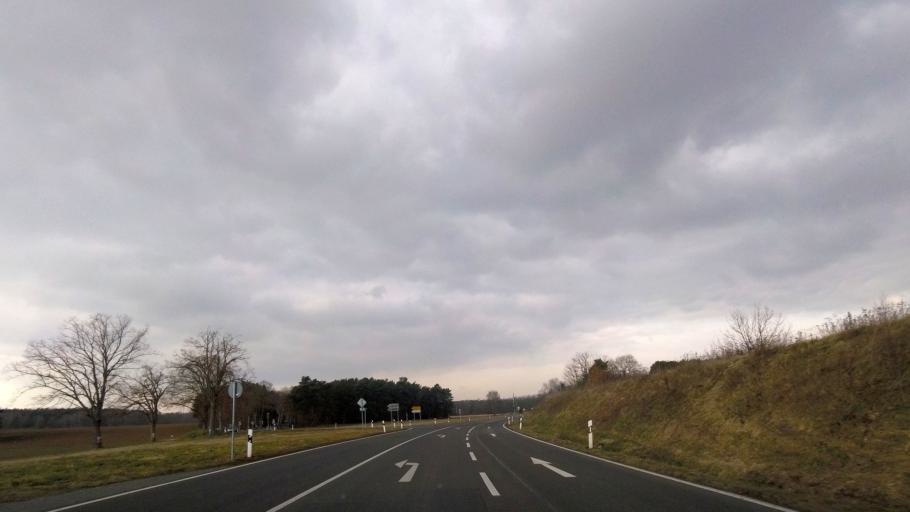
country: DE
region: Brandenburg
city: Belzig
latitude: 52.1322
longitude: 12.6263
